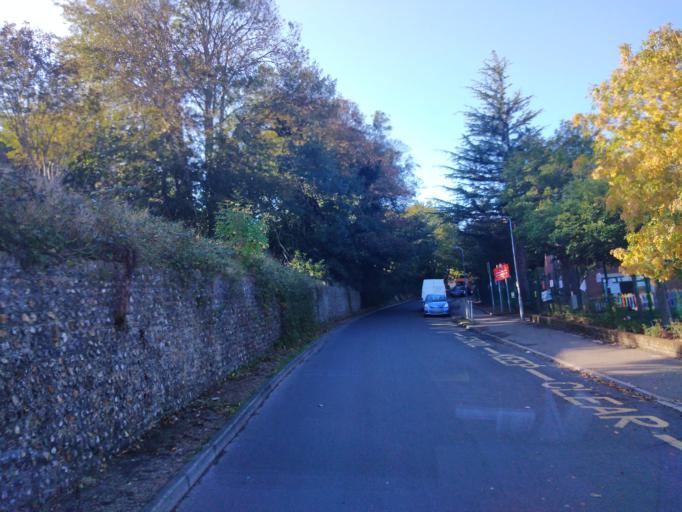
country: GB
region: England
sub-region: East Sussex
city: Newhaven
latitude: 50.7922
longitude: 0.0453
